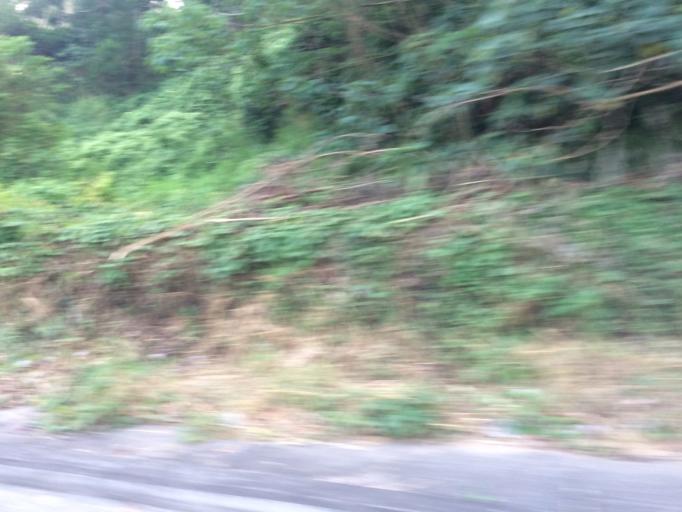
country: TW
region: Taiwan
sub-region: Hsinchu
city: Hsinchu
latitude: 24.7172
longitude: 120.9156
